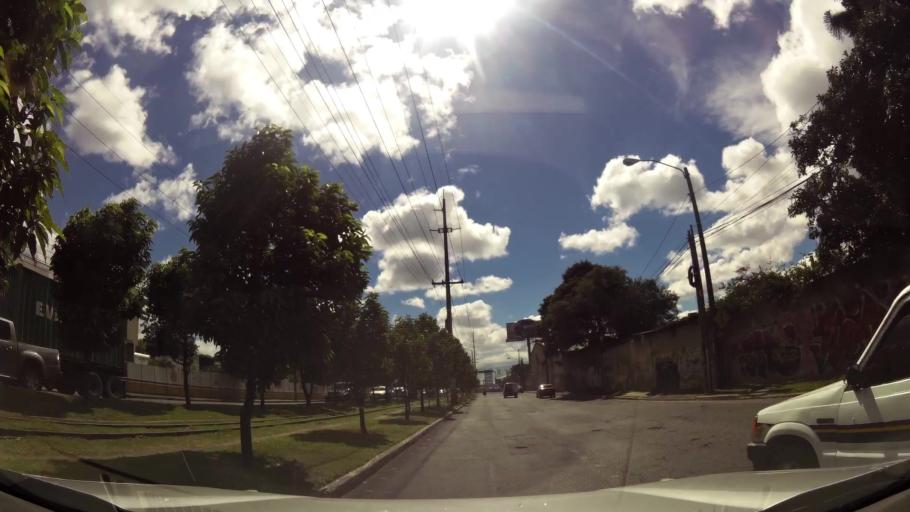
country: GT
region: Guatemala
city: Santa Catarina Pinula
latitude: 14.5848
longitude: -90.5427
